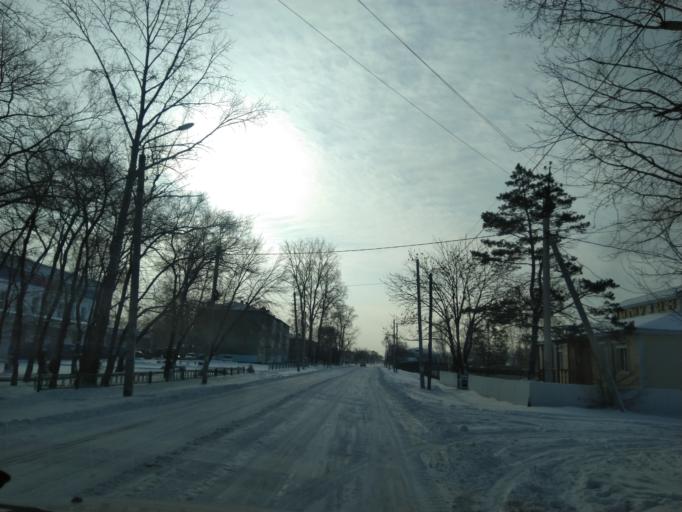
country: RU
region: Amur
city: Poyarkovo
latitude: 49.6252
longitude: 128.6505
